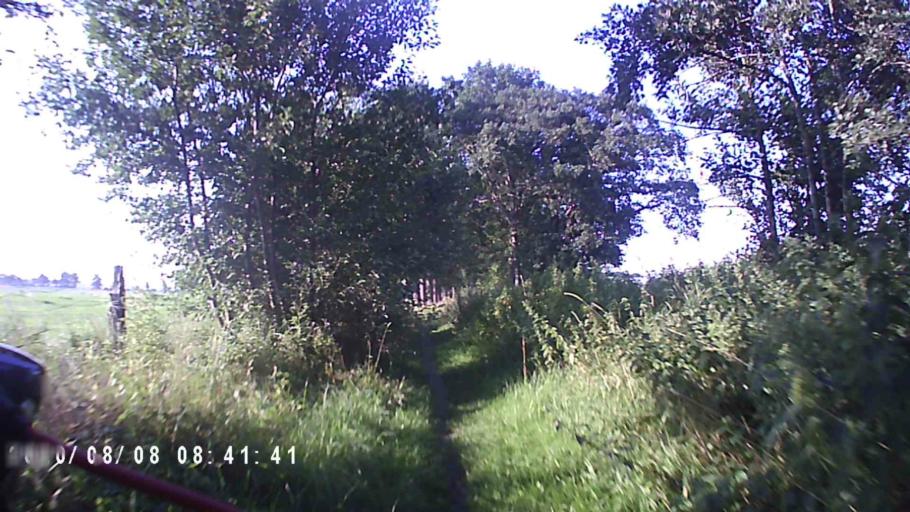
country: NL
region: Groningen
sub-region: Gemeente Leek
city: Leek
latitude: 53.0669
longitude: 6.3604
